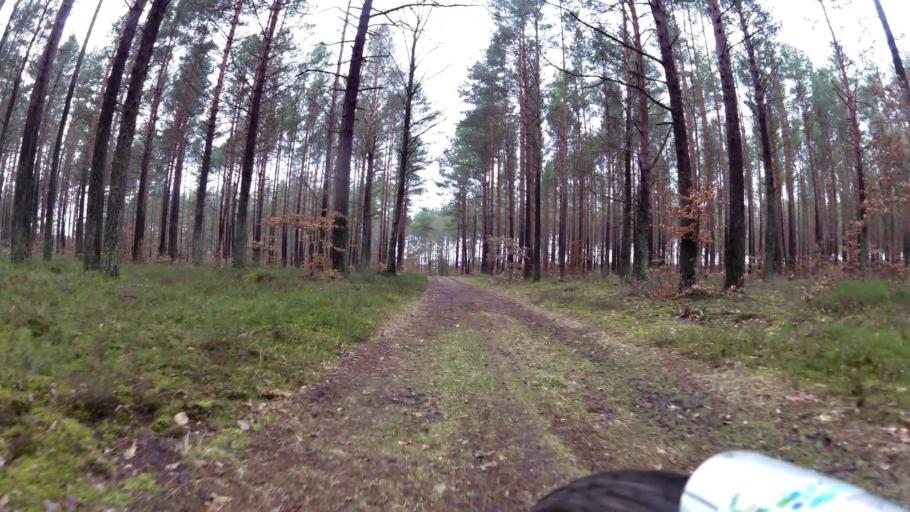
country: PL
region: Pomeranian Voivodeship
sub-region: Powiat bytowski
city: Kolczyglowy
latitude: 54.2398
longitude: 17.2518
